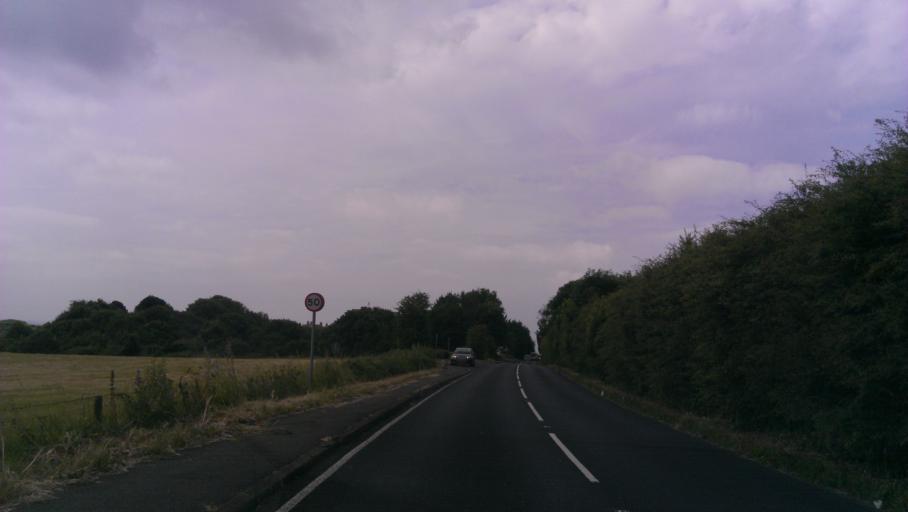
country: GB
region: England
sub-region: Kent
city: Dover
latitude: 51.1360
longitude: 1.3252
